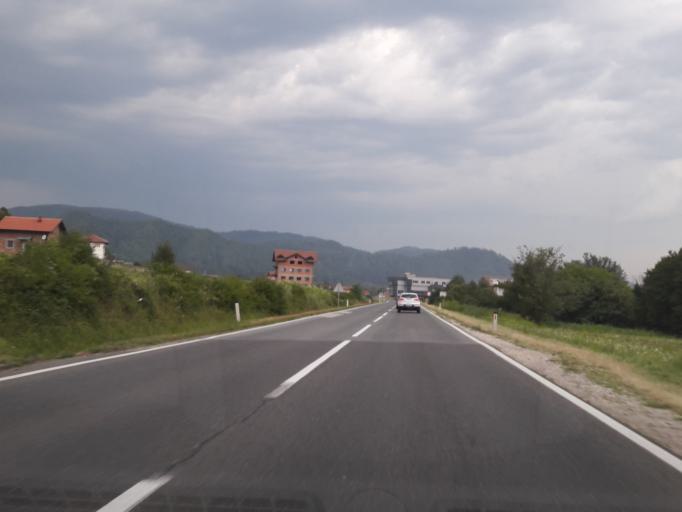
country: BA
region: Federation of Bosnia and Herzegovina
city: Maglaj
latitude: 44.5852
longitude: 18.0970
